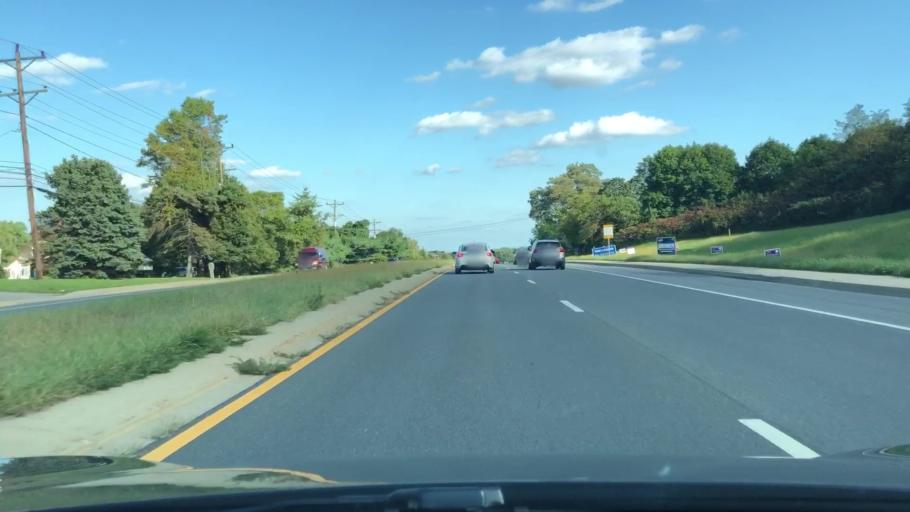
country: US
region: Delaware
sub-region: New Castle County
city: Claymont
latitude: 39.8257
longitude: -75.5073
